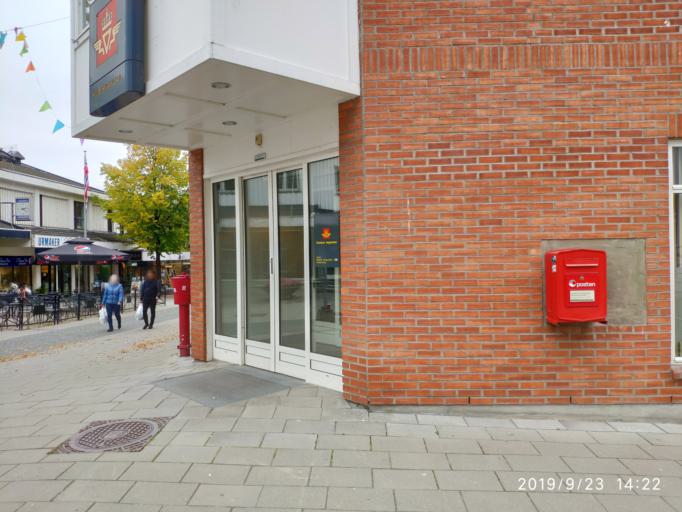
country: NO
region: Oppland
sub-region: Gjovik
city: Gjovik
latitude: 60.7947
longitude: 10.6892
